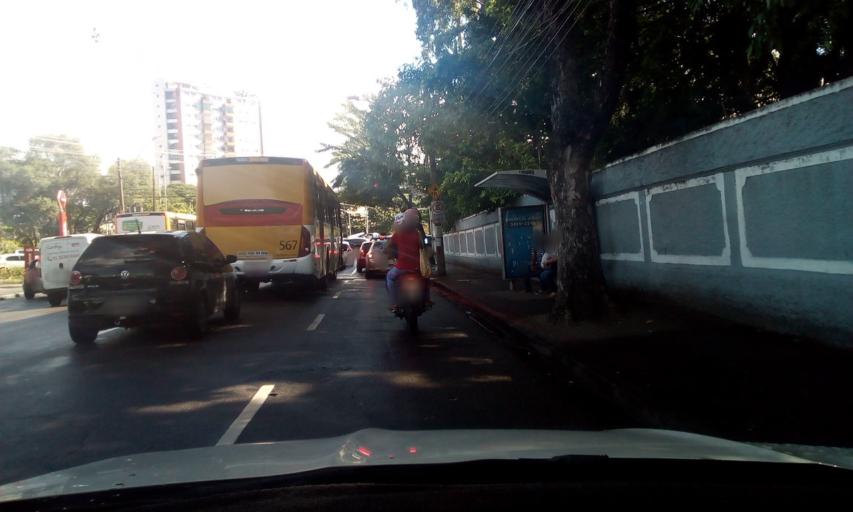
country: BR
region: Pernambuco
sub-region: Recife
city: Recife
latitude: -8.0542
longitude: -34.8960
